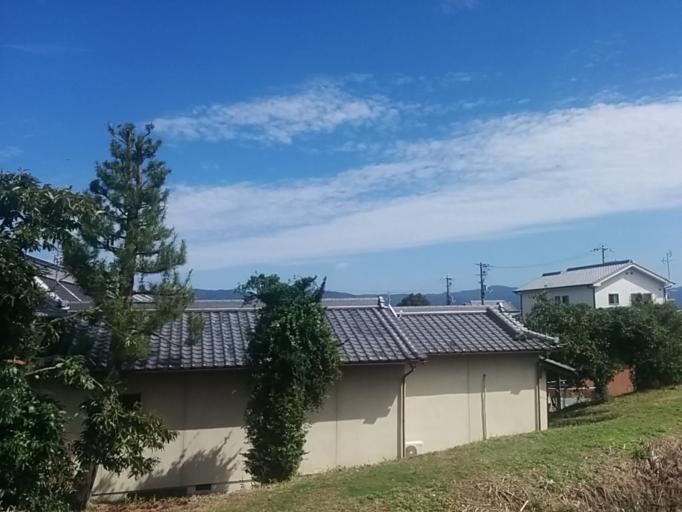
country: JP
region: Nara
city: Nara-shi
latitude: 34.6738
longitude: 135.7833
